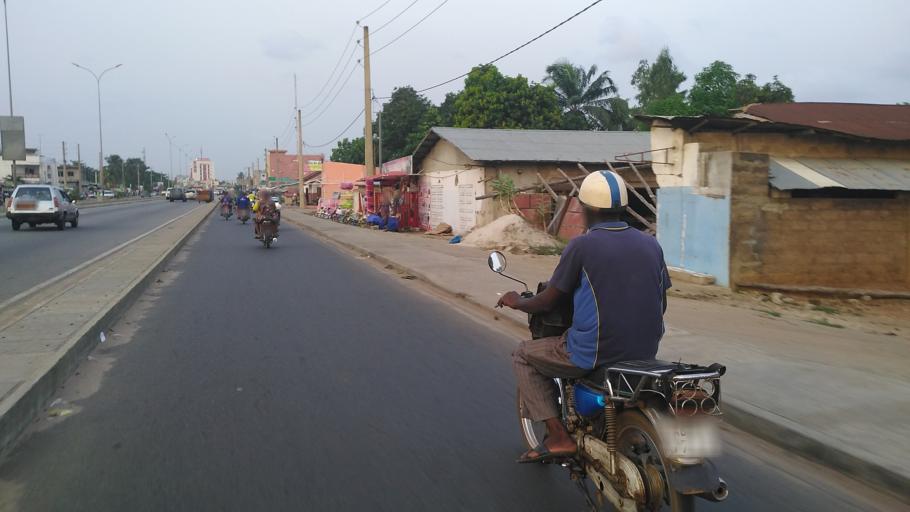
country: BJ
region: Atlantique
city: Abomey-Calavi
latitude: 6.4367
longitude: 2.3522
